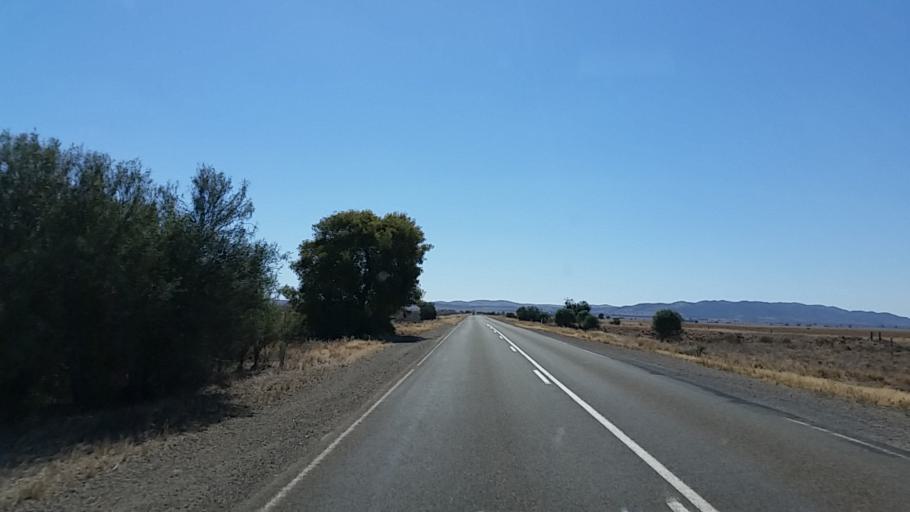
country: AU
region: South Australia
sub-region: Peterborough
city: Peterborough
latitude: -32.6657
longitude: 138.6070
